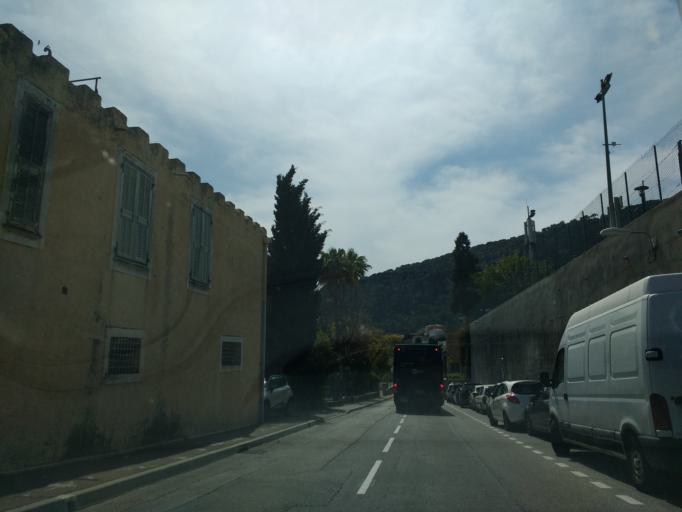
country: FR
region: Provence-Alpes-Cote d'Azur
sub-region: Departement des Alpes-Maritimes
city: Villefranche-sur-Mer
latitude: 43.7014
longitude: 7.3093
